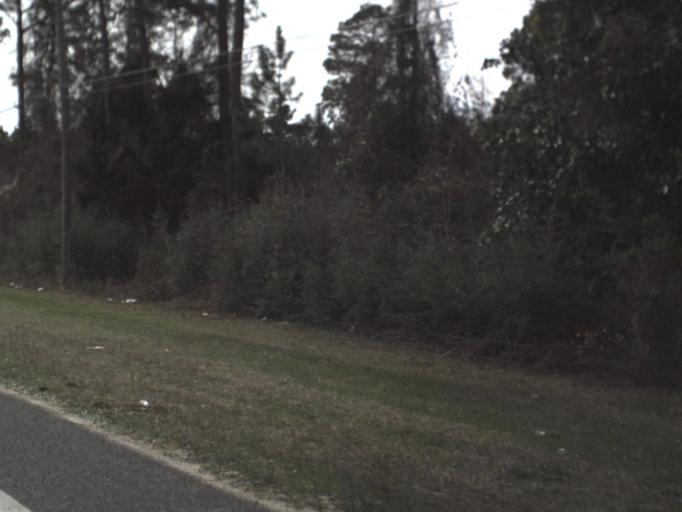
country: US
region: Florida
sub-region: Bay County
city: Hiland Park
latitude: 30.2697
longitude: -85.5278
